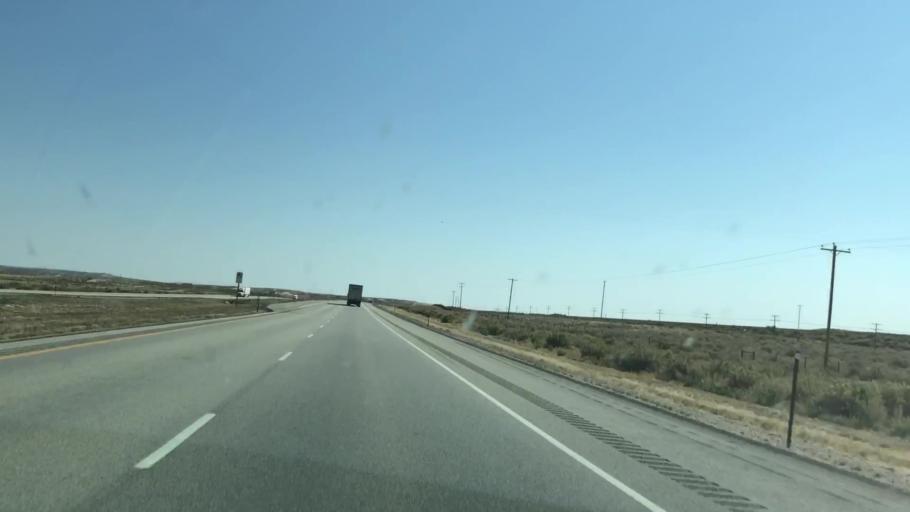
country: US
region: Wyoming
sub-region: Carbon County
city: Rawlins
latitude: 41.7013
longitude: -107.9057
